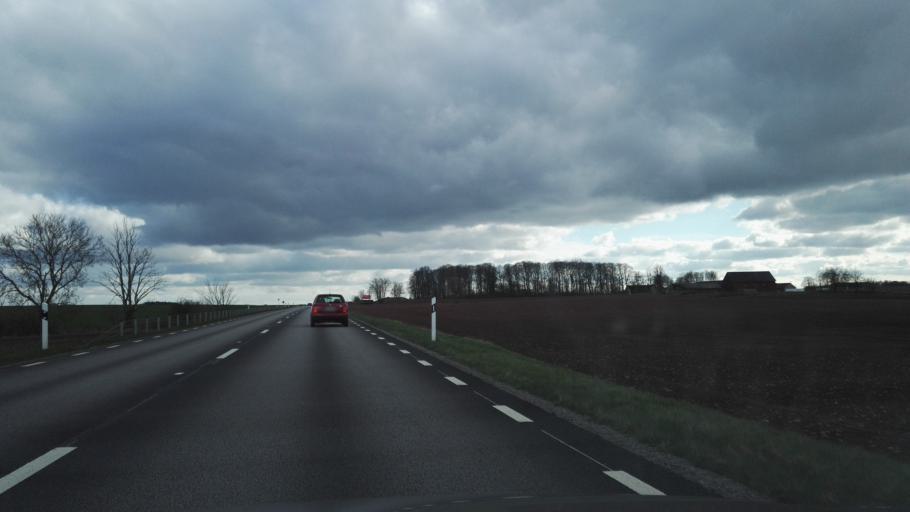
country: SE
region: Skane
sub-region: Sjobo Kommun
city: Sjoebo
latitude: 55.6765
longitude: 13.7158
